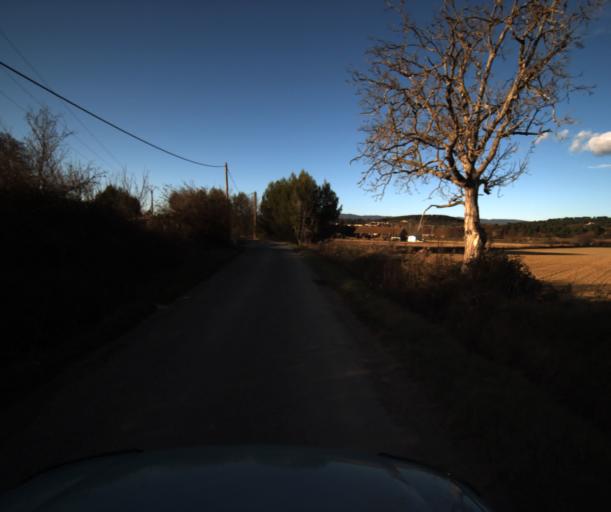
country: FR
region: Provence-Alpes-Cote d'Azur
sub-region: Departement du Vaucluse
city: Pertuis
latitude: 43.6722
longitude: 5.5293
